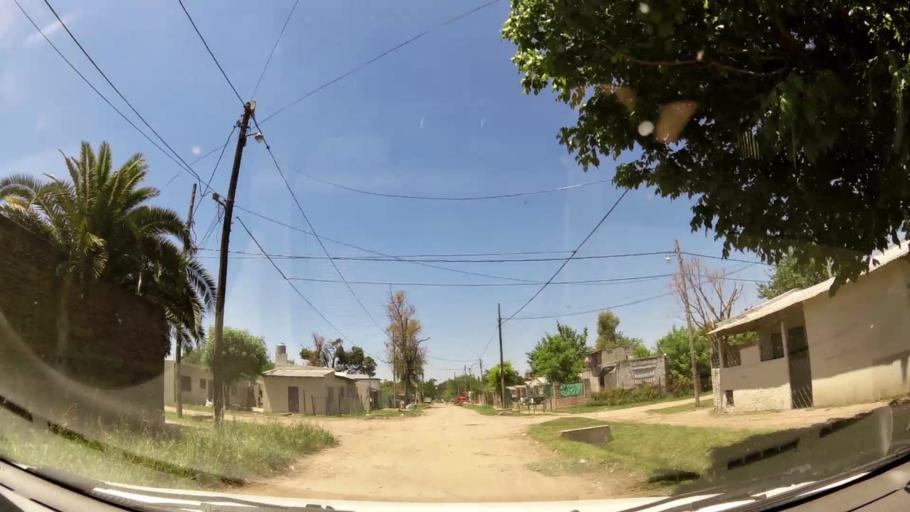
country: AR
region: Buenos Aires
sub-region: Partido de Merlo
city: Merlo
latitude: -34.6548
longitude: -58.7077
